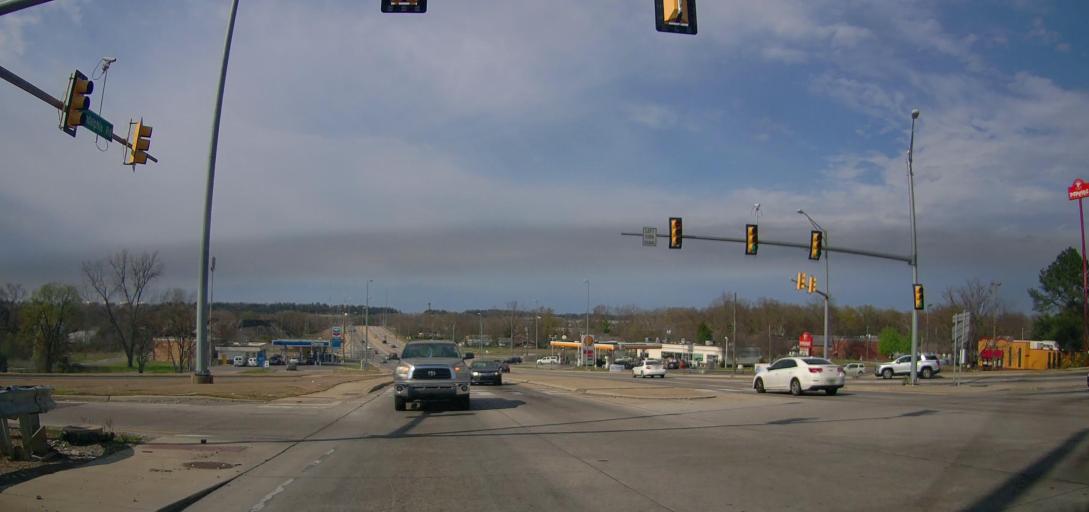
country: US
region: Alabama
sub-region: Jefferson County
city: Birmingham
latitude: 33.5216
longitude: -86.8496
